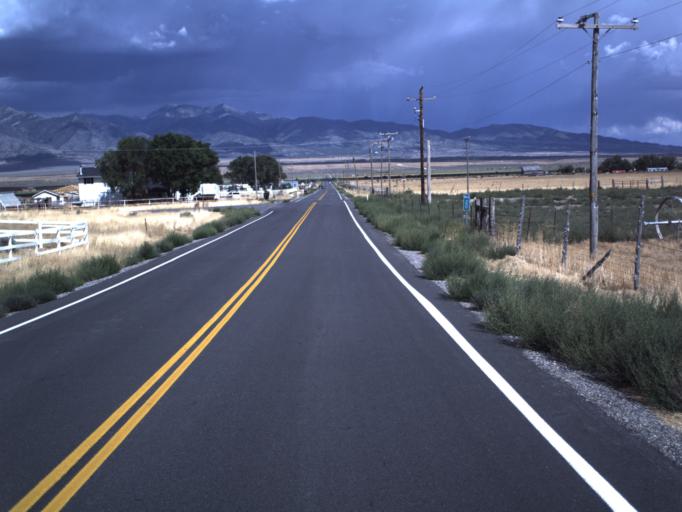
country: US
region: Utah
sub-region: Tooele County
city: Tooele
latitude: 40.3366
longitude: -112.4472
